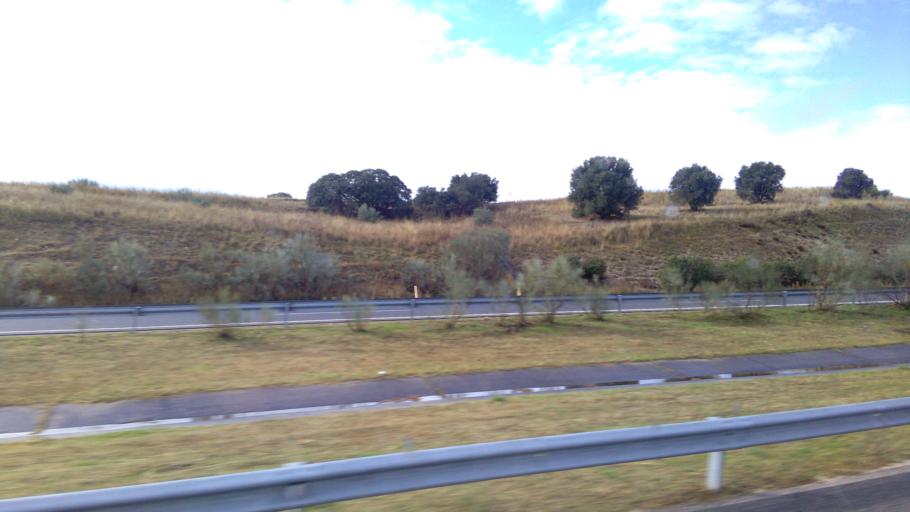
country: ES
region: Madrid
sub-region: Provincia de Madrid
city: El Alamo
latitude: 40.2624
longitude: -3.9945
